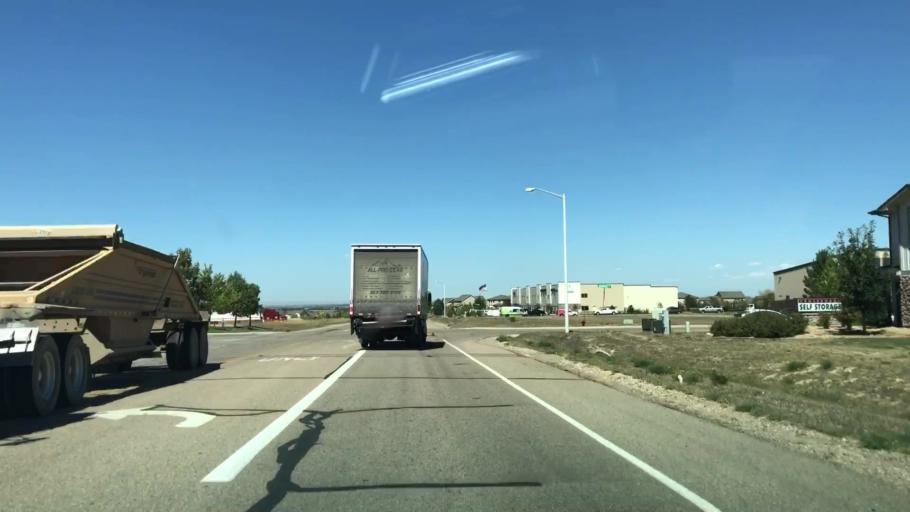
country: US
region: Colorado
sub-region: Weld County
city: Windsor
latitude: 40.4369
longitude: -104.9676
